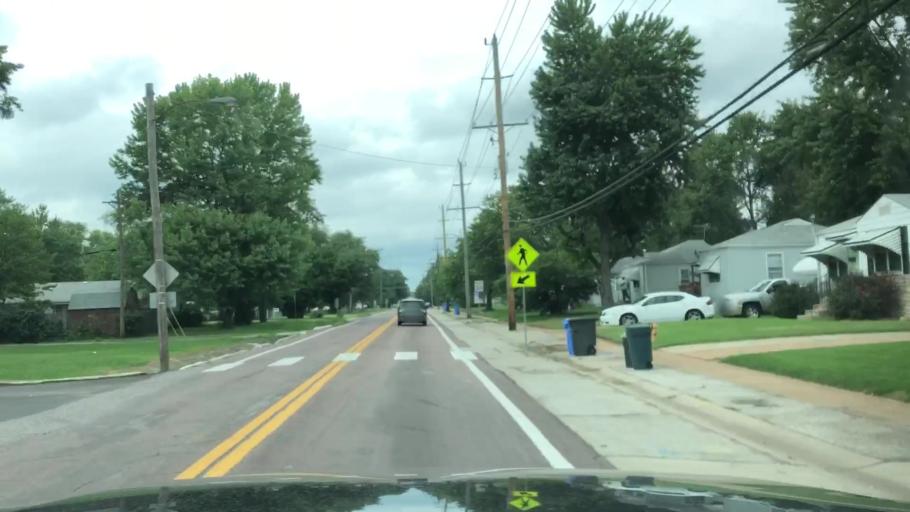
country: US
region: Missouri
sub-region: Saint Louis County
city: Florissant
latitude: 38.8000
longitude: -90.3439
